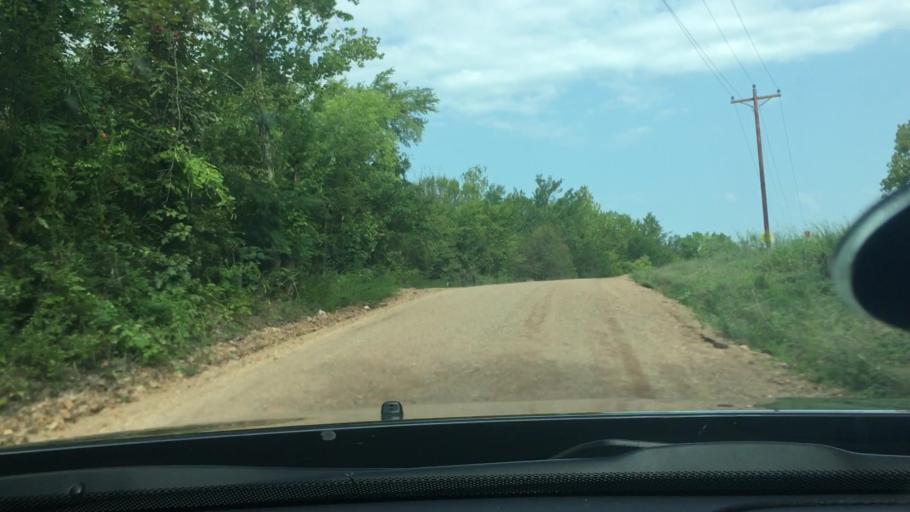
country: US
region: Oklahoma
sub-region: Atoka County
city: Atoka
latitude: 34.4398
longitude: -96.0639
